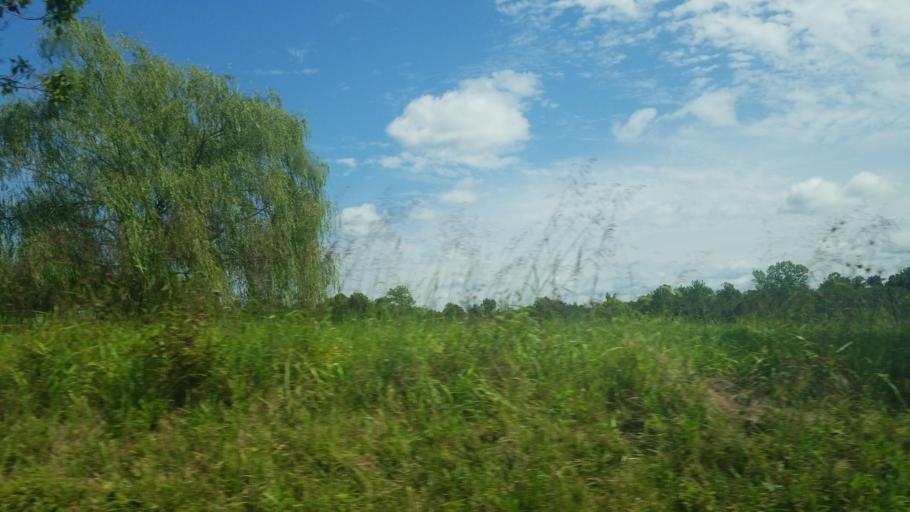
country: US
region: Illinois
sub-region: Williamson County
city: Johnston City
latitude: 37.7773
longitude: -88.8130
